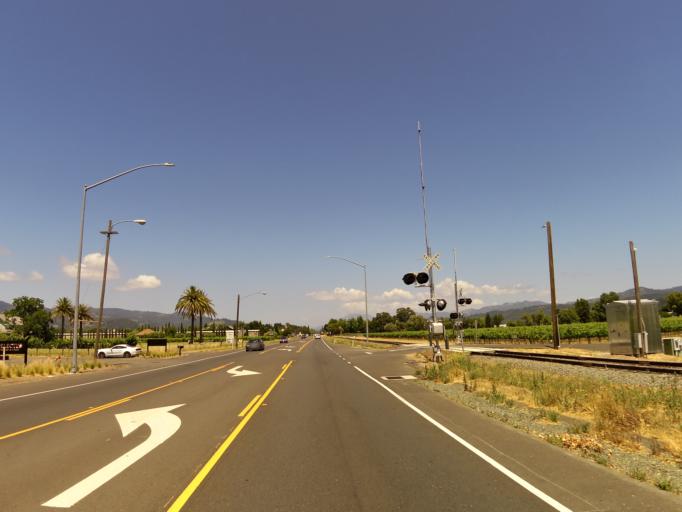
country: US
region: California
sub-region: Napa County
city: Saint Helena
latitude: 38.4851
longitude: -122.4454
